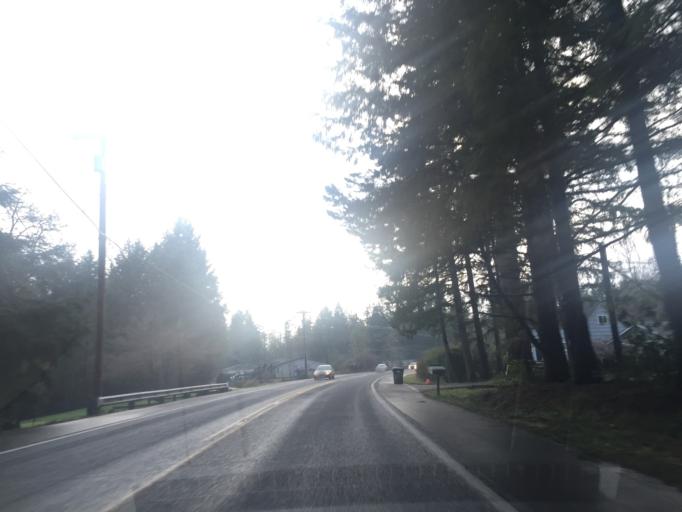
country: US
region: Washington
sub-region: Thurston County
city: Olympia
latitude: 47.0941
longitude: -122.8896
